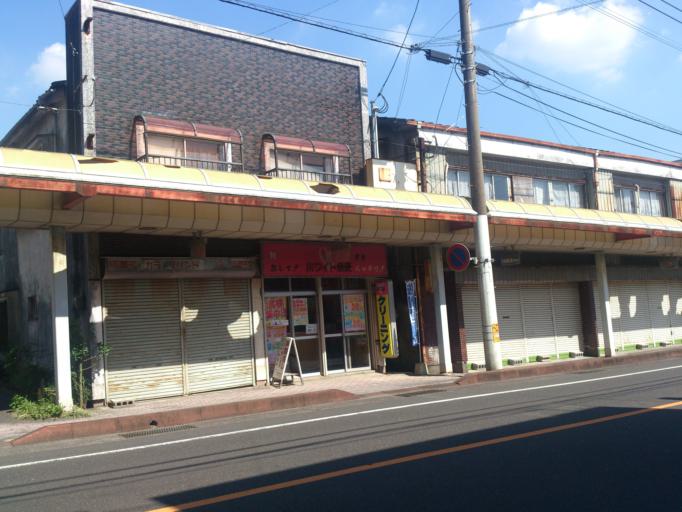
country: JP
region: Kagoshima
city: Kanoya
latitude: 31.3835
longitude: 130.8520
